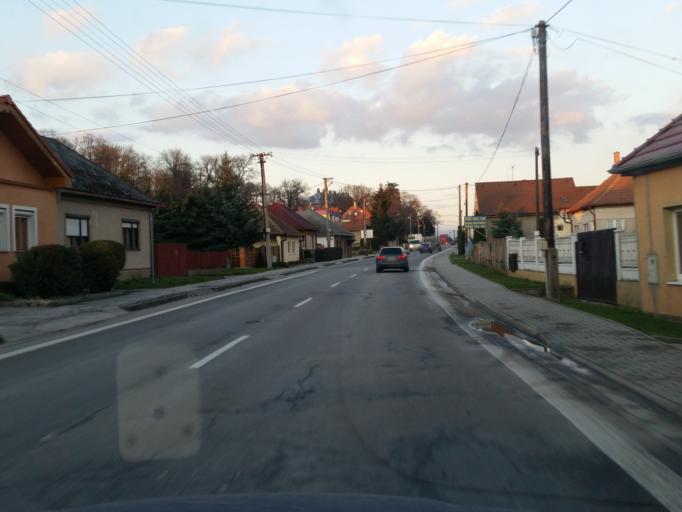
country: SK
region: Nitriansky
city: Banovce nad Bebravou
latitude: 48.5900
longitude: 18.2035
